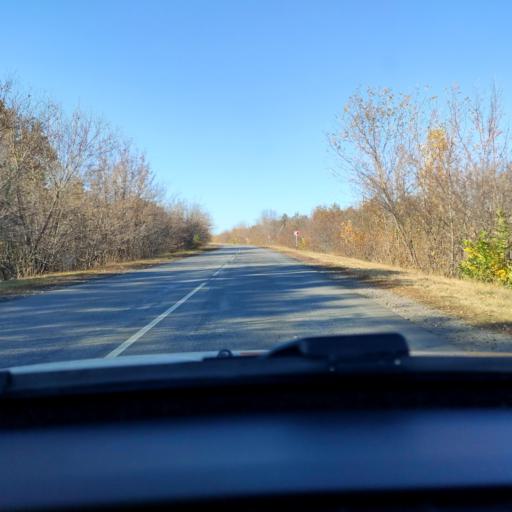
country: RU
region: Voronezj
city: Latnaya
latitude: 51.8002
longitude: 38.8706
